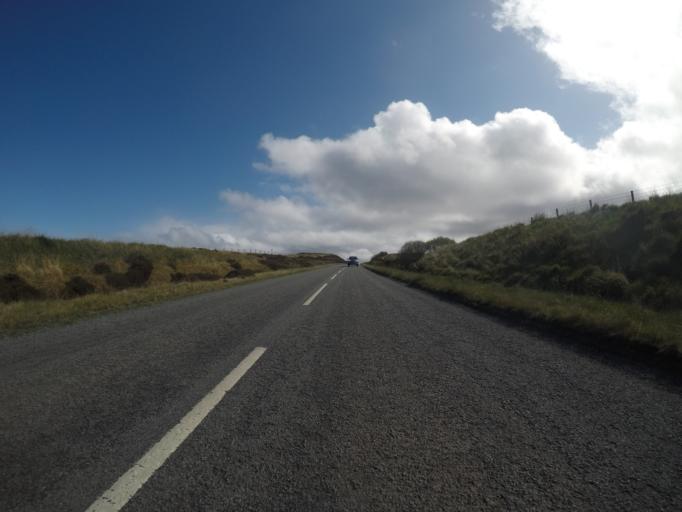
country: GB
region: Scotland
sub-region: Highland
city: Portree
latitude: 57.5731
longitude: -6.1541
